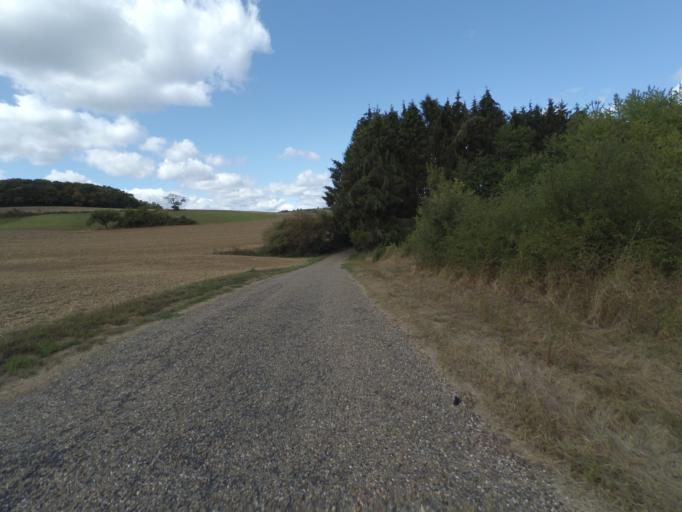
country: LU
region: Grevenmacher
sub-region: Canton de Remich
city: Lenningen
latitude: 49.6129
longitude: 6.3679
